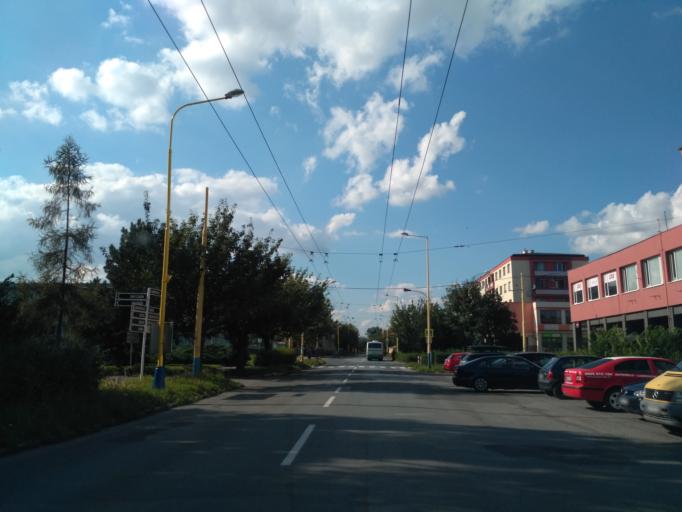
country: SK
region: Presovsky
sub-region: Okres Presov
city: Presov
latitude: 48.9892
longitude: 21.2363
